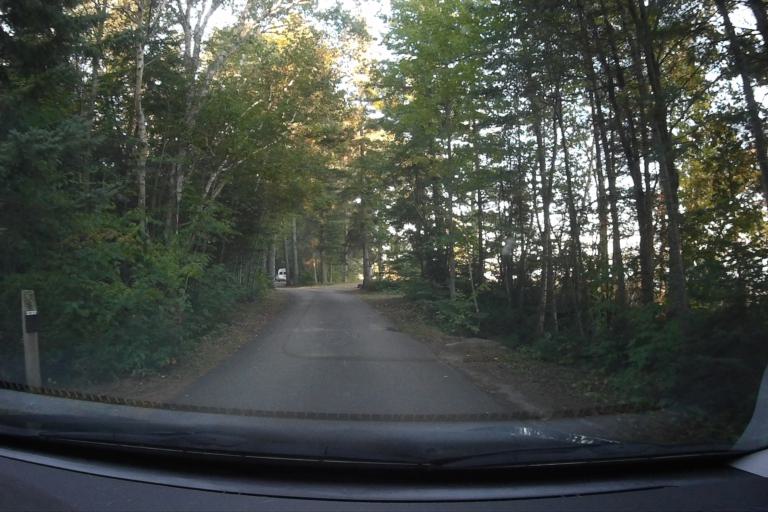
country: CA
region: Ontario
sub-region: Algoma
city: Sault Ste. Marie
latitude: 46.9691
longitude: -84.6915
